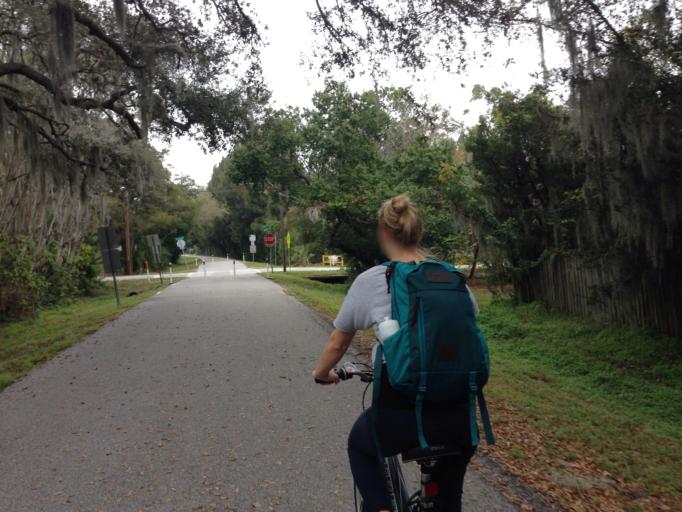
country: US
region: Florida
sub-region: Pinellas County
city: Dunedin
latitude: 27.9969
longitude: -82.7889
